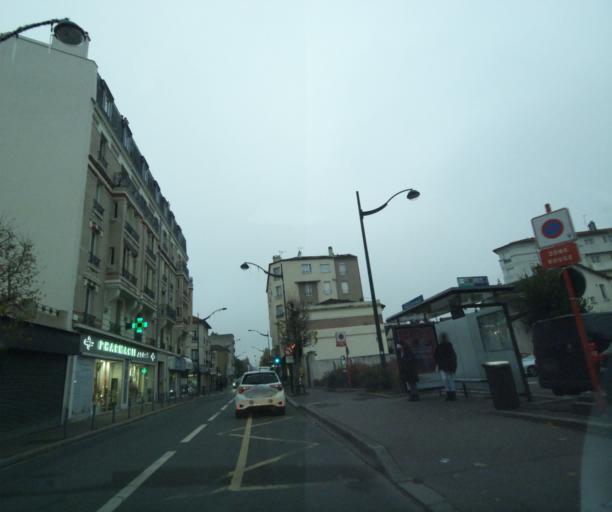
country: FR
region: Ile-de-France
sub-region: Departement de Seine-Saint-Denis
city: Les Pavillons-sous-Bois
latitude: 48.9045
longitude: 2.5041
